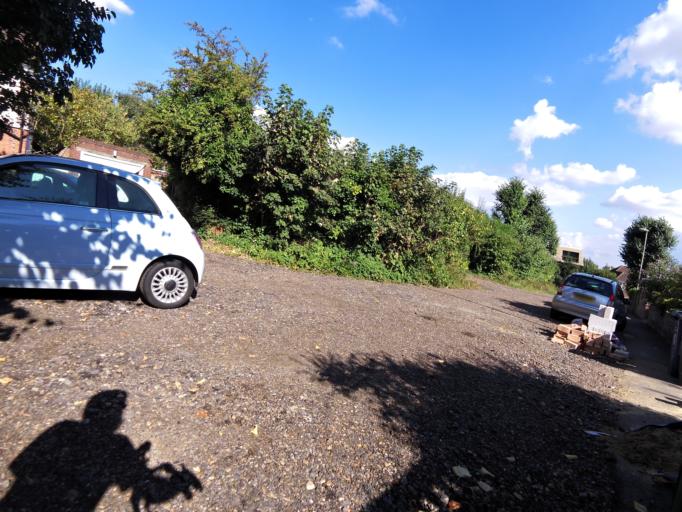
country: GB
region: England
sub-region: Greater London
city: Barnet
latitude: 51.6445
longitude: -0.1793
